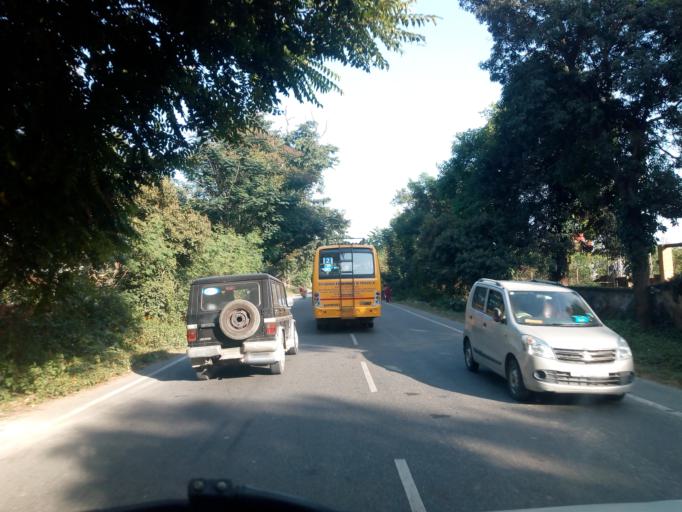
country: IN
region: Uttarakhand
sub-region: Dehradun
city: Dehradun
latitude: 30.3453
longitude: 77.9047
